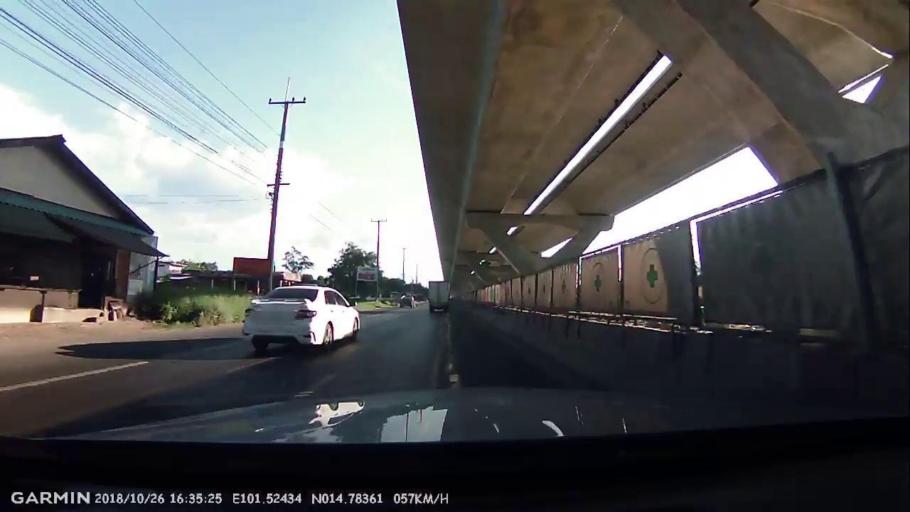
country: TH
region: Nakhon Ratchasima
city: Pak Chong
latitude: 14.7834
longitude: 101.5243
